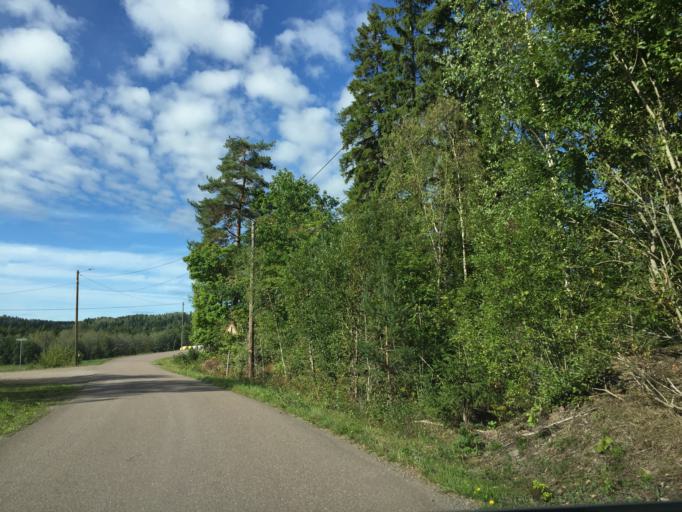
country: NO
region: Vestfold
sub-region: Holmestrand
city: Gullhaug
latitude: 59.4767
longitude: 10.1831
